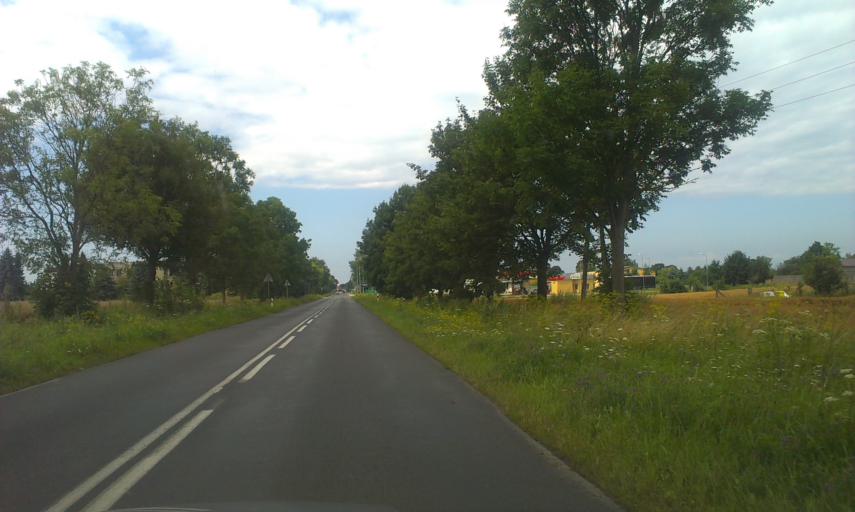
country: PL
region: West Pomeranian Voivodeship
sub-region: Powiat kolobrzeski
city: Dygowo
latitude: 54.1259
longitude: 15.7296
